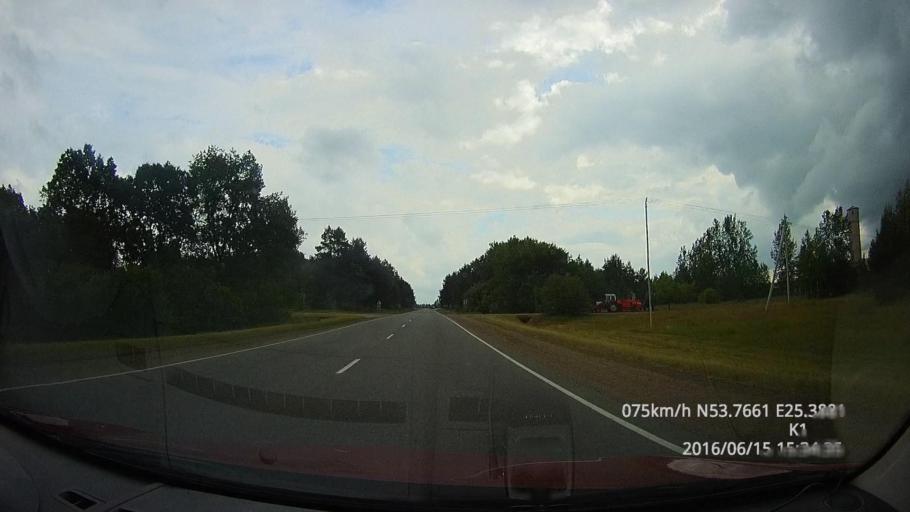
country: BY
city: Berezovka
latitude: 53.7655
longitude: 25.3884
